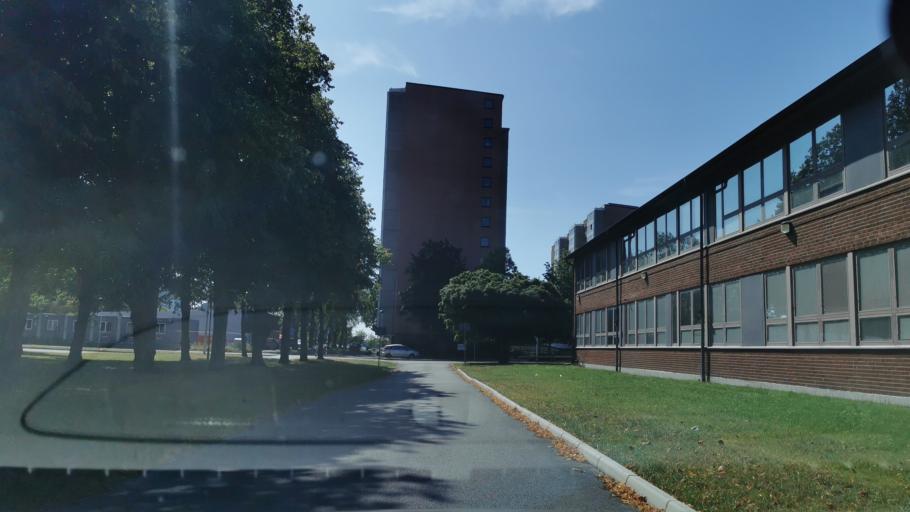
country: SE
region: Vaestra Goetaland
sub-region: Goteborg
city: Majorna
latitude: 57.6577
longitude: 11.9151
